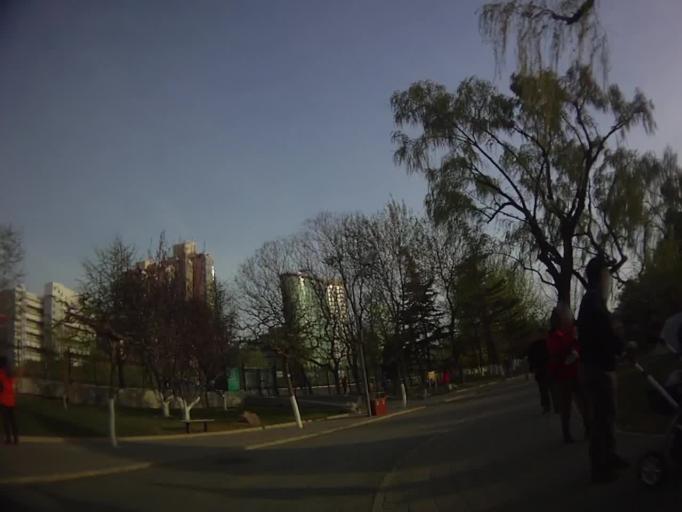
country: CN
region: Beijing
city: Longtan
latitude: 39.8769
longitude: 116.4385
